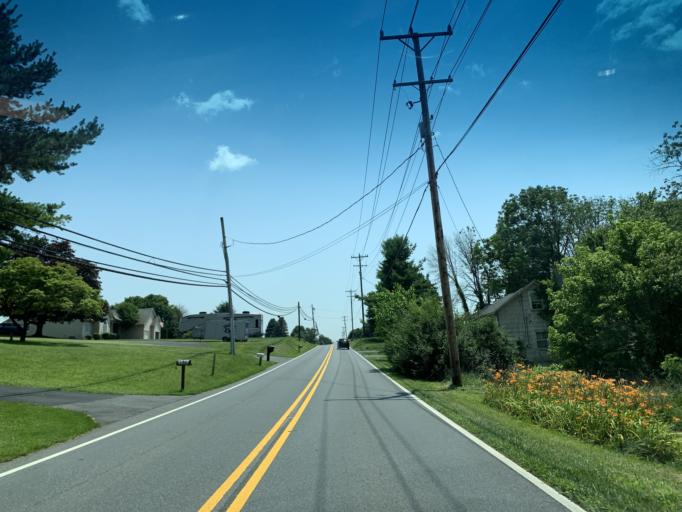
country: US
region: Maryland
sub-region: Frederick County
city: Green Valley
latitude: 39.3597
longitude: -77.2695
